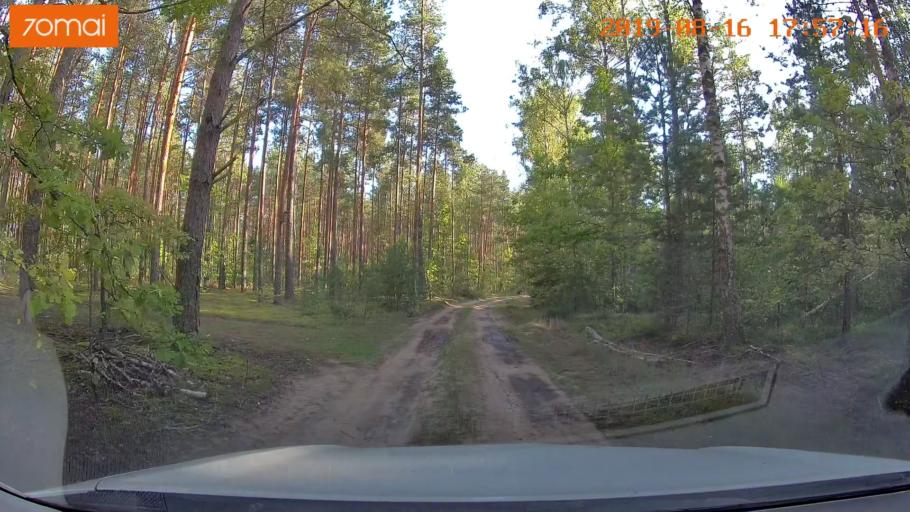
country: BY
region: Mogilev
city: Asipovichy
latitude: 53.2239
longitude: 28.6589
